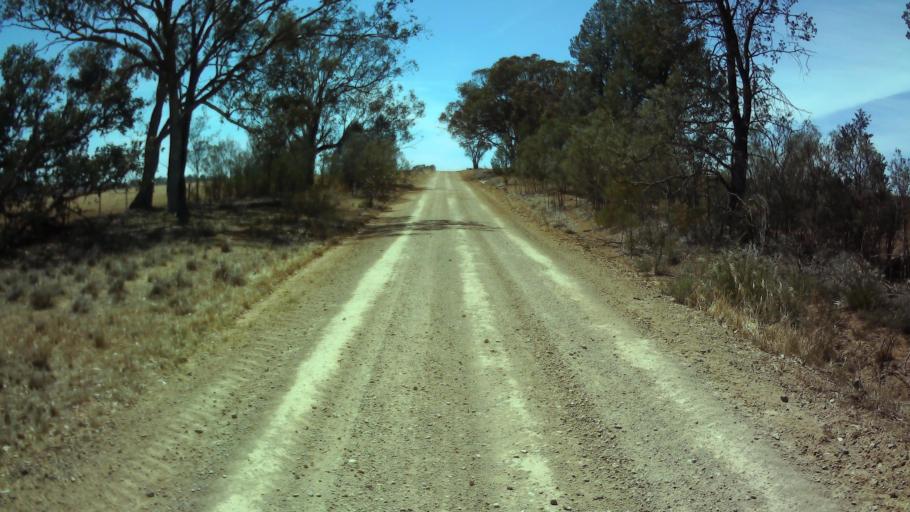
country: AU
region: New South Wales
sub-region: Weddin
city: Grenfell
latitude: -33.9440
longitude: 148.1513
